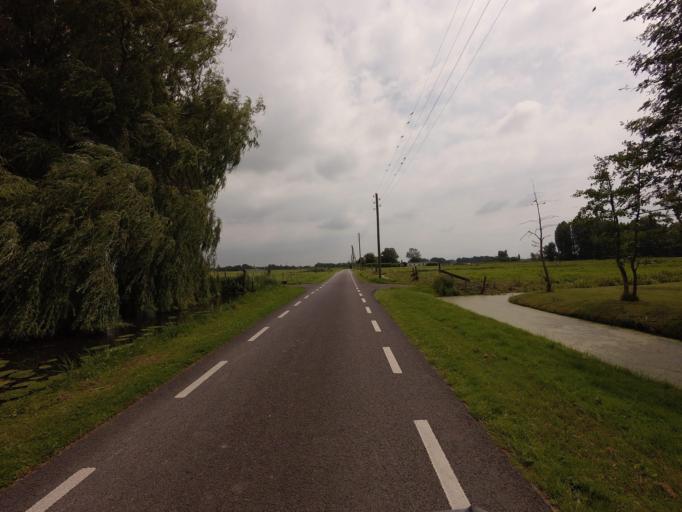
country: NL
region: South Holland
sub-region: Gemeente Waddinxveen
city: Waddinxveen
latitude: 51.9880
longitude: 4.6438
